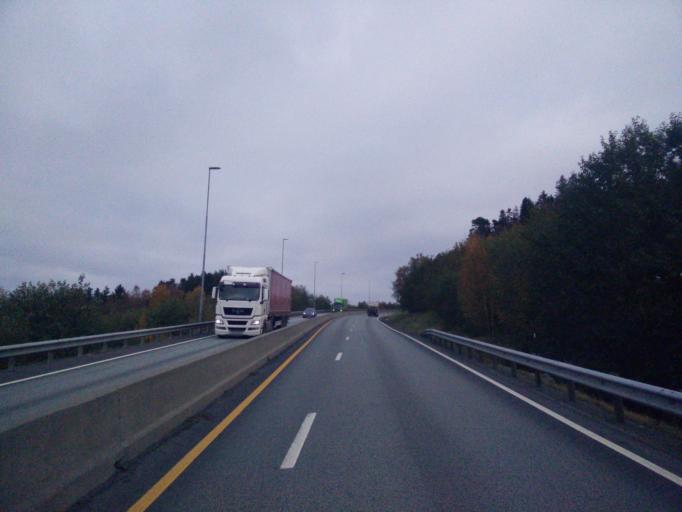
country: NO
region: Sor-Trondelag
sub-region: Malvik
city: Malvik
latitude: 63.4239
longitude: 10.5622
